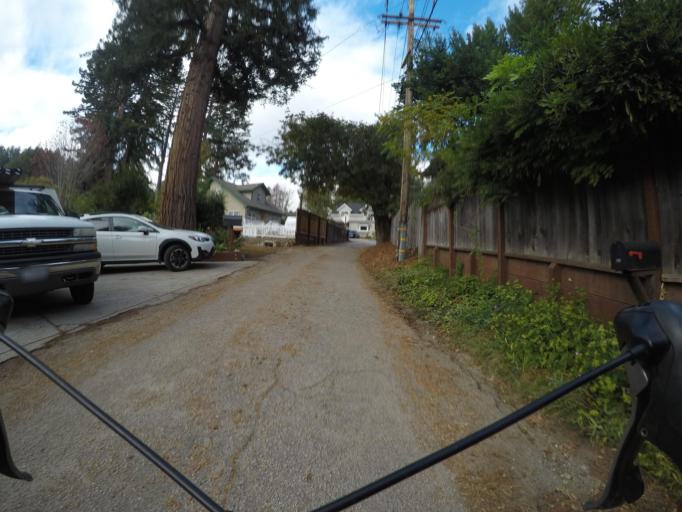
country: US
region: California
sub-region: Santa Cruz County
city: Ben Lomond
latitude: 37.0833
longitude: -122.0820
